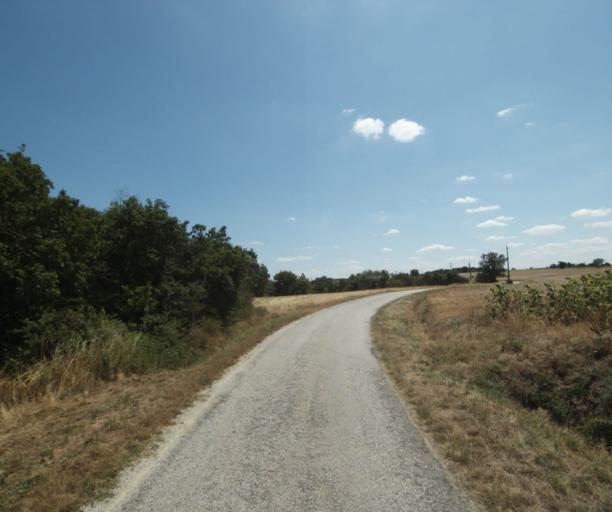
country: FR
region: Midi-Pyrenees
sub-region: Departement de la Haute-Garonne
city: Auriac-sur-Vendinelle
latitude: 43.4940
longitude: 1.8557
